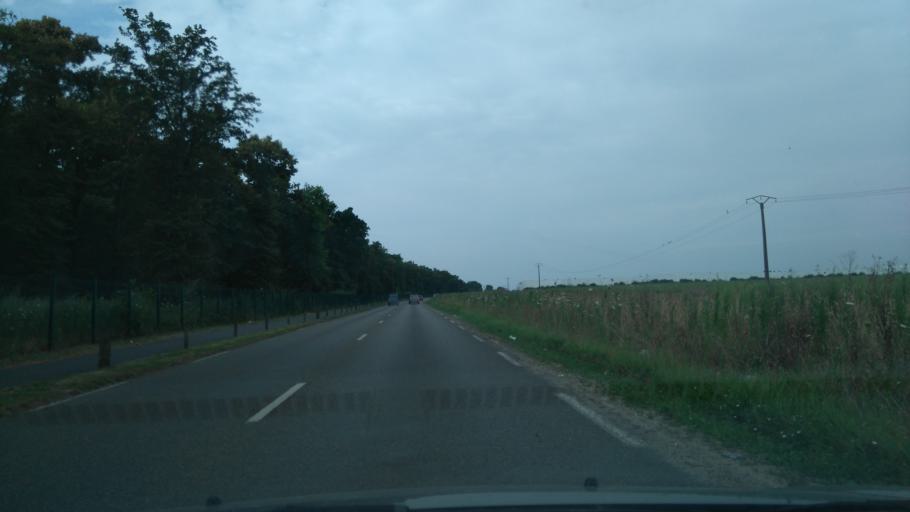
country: FR
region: Picardie
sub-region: Departement de l'Oise
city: Saint-Maximin
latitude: 49.2263
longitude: 2.4561
